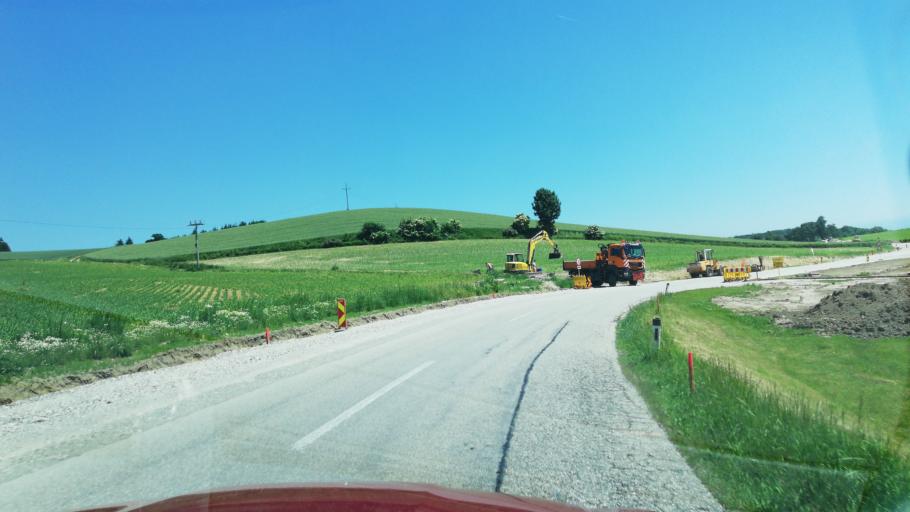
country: AT
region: Upper Austria
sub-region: Wels-Land
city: Bachmanning
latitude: 48.1315
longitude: 13.7690
